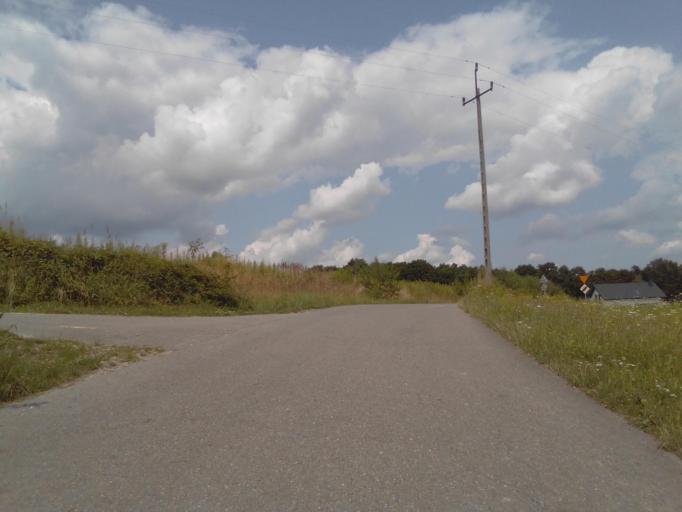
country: PL
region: Subcarpathian Voivodeship
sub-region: Powiat strzyzowski
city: Frysztak
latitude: 49.8210
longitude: 21.5945
